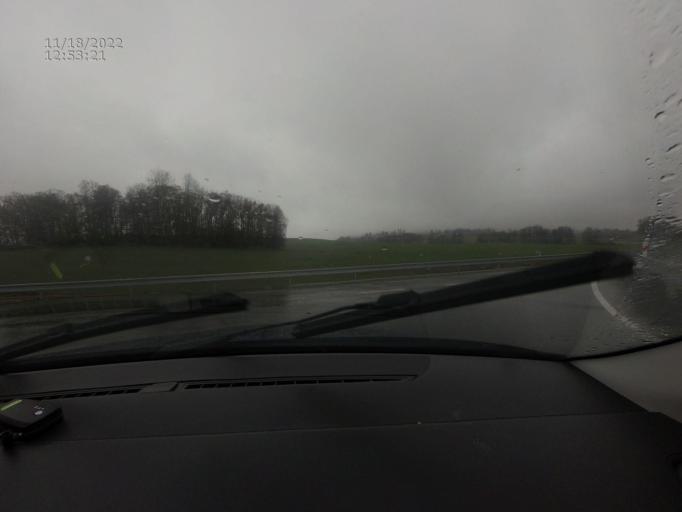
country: CZ
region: Plzensky
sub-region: Okres Klatovy
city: Kolinec
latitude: 49.3244
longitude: 13.4423
